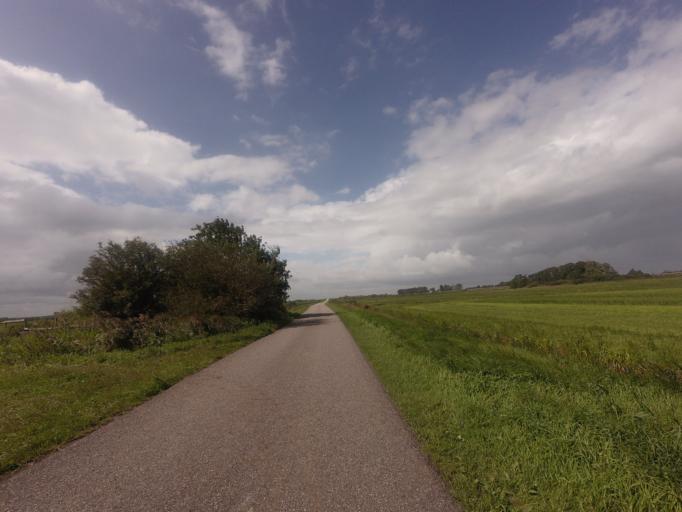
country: NL
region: Friesland
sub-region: Gemeente Skarsterlan
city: Sint Nicolaasga
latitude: 52.9765
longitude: 5.7405
